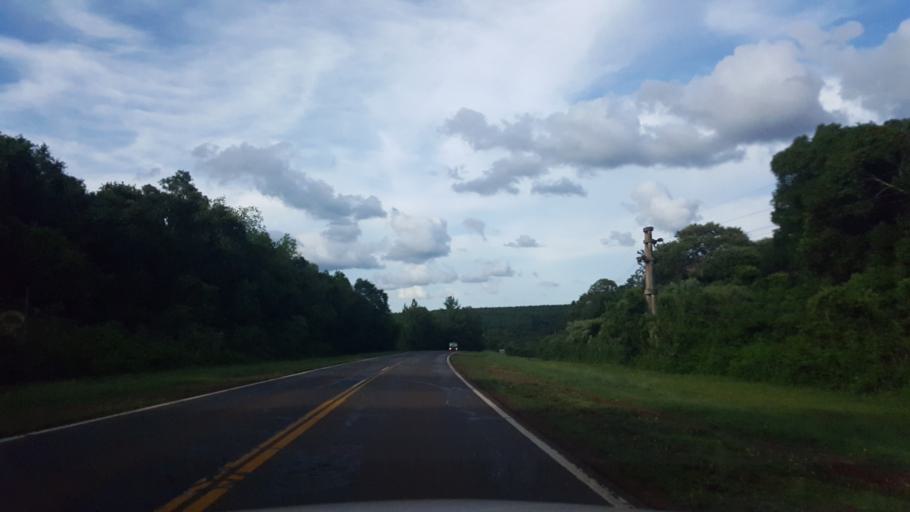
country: AR
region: Misiones
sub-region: Departamento de San Ignacio
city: San Ignacio
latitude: -27.2350
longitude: -55.5169
